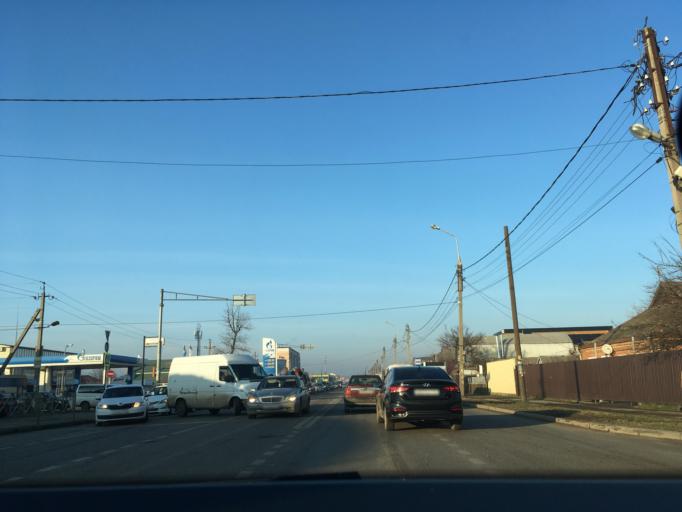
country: RU
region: Krasnodarskiy
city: Krasnodar
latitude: 45.1107
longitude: 39.0123
